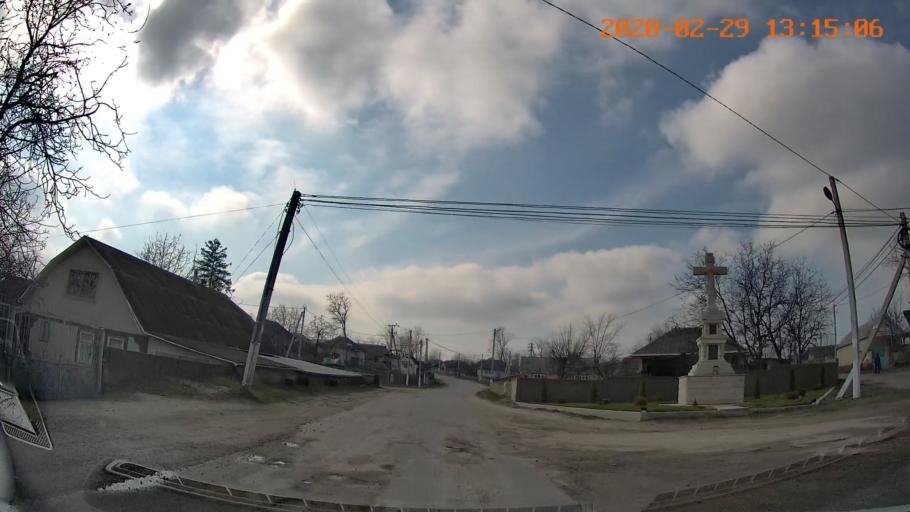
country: MD
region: Telenesti
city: Camenca
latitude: 48.0112
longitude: 28.6722
